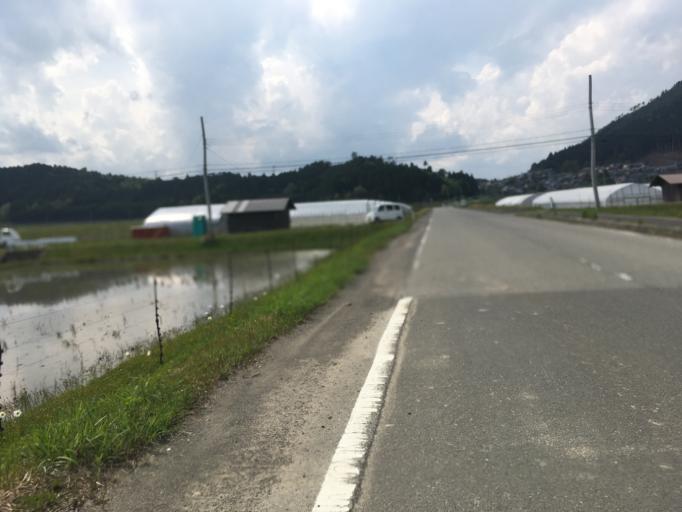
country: JP
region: Kyoto
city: Kameoka
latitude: 35.1045
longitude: 135.5862
